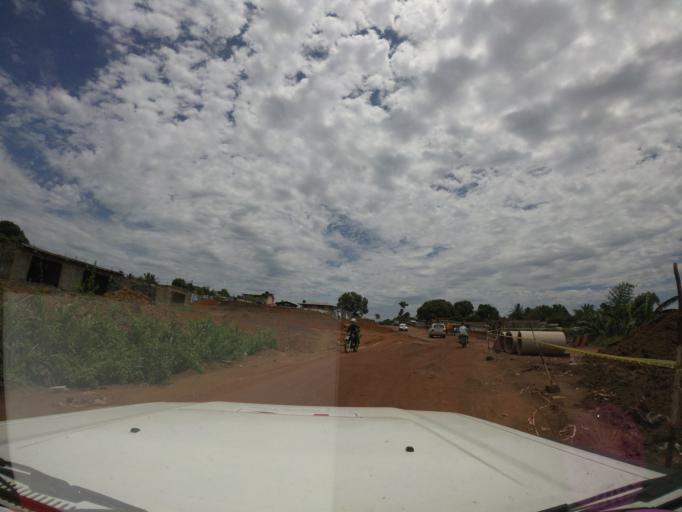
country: LR
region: Margibi
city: Kakata
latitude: 6.5362
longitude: -10.3452
